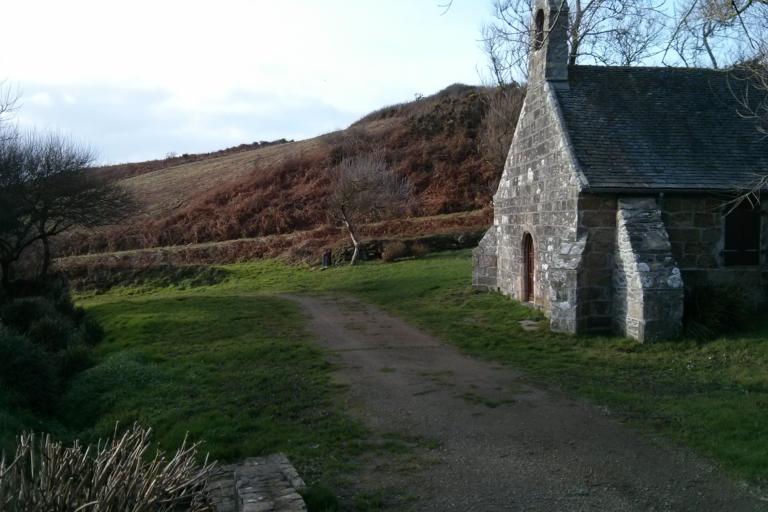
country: FR
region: Brittany
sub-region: Departement du Finistere
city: Le Conquet
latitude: 48.3990
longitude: -4.7725
